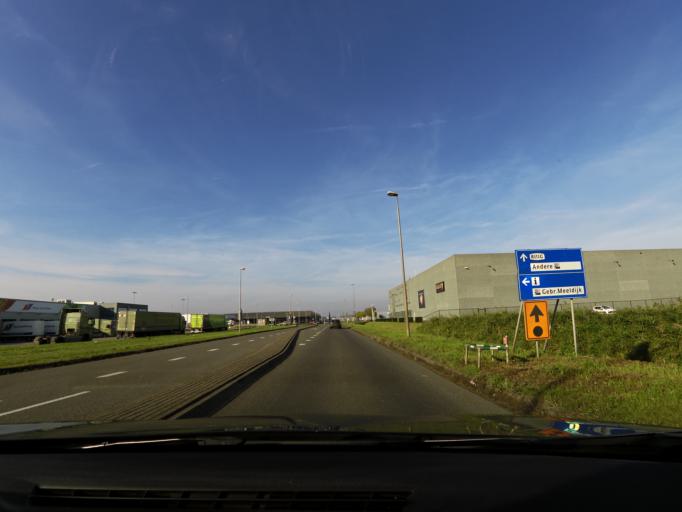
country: NL
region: South Holland
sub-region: Gemeente Zwijndrecht
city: Heerjansdam
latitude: 51.8568
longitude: 4.5621
